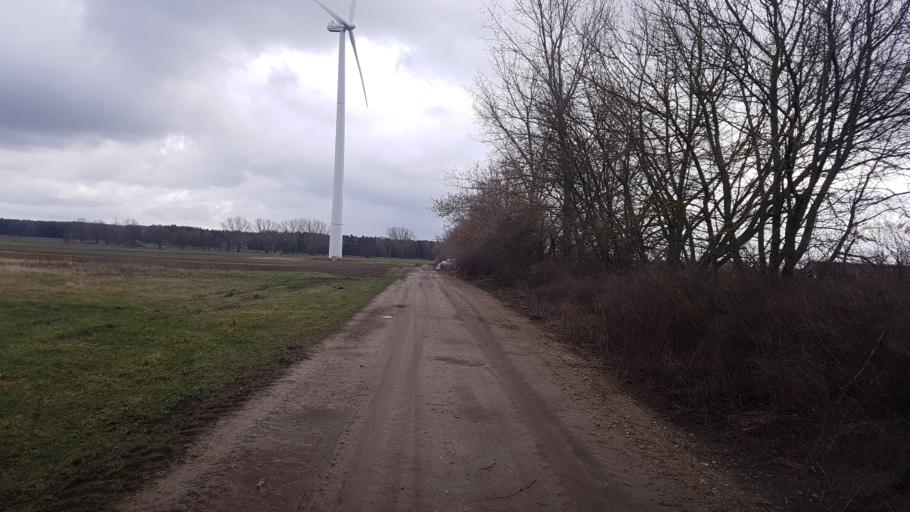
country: DE
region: Brandenburg
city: Bronkow
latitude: 51.6439
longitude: 13.8750
